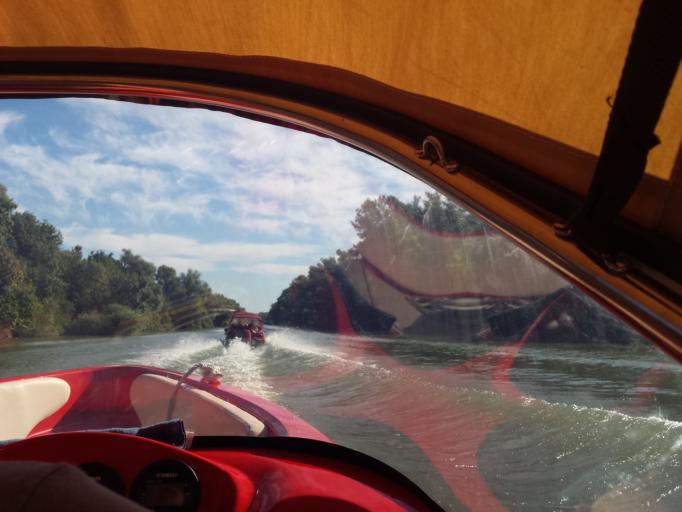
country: RO
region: Tulcea
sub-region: Comuna Nufaru
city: Malcoci
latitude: 45.2147
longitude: 28.8677
